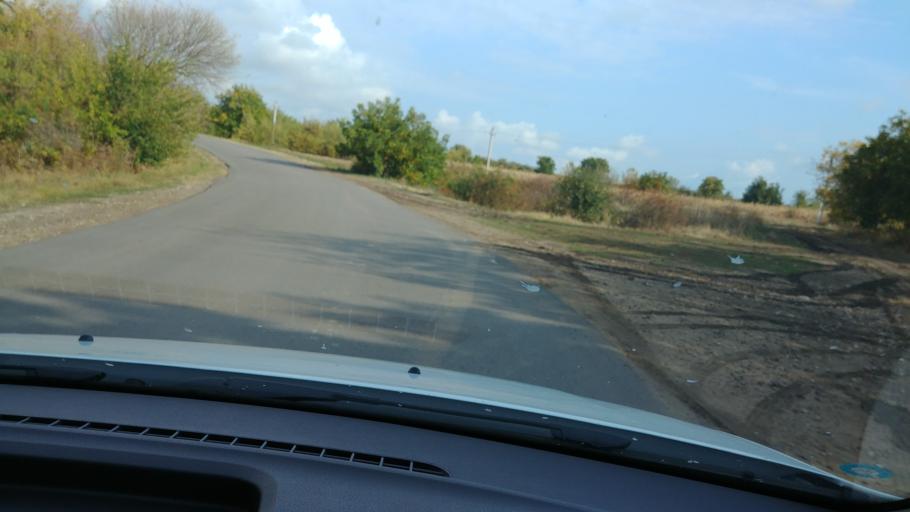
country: MD
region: Criuleni
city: Criuleni
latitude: 47.2147
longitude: 29.0680
